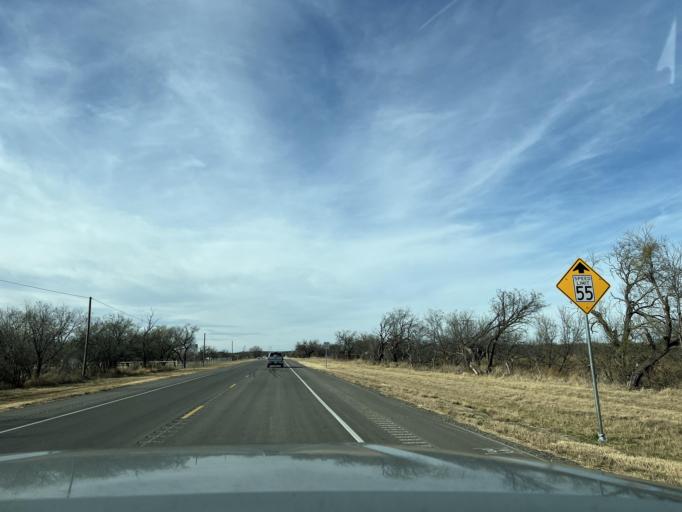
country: US
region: Texas
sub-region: Shackelford County
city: Albany
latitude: 32.7151
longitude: -99.2829
